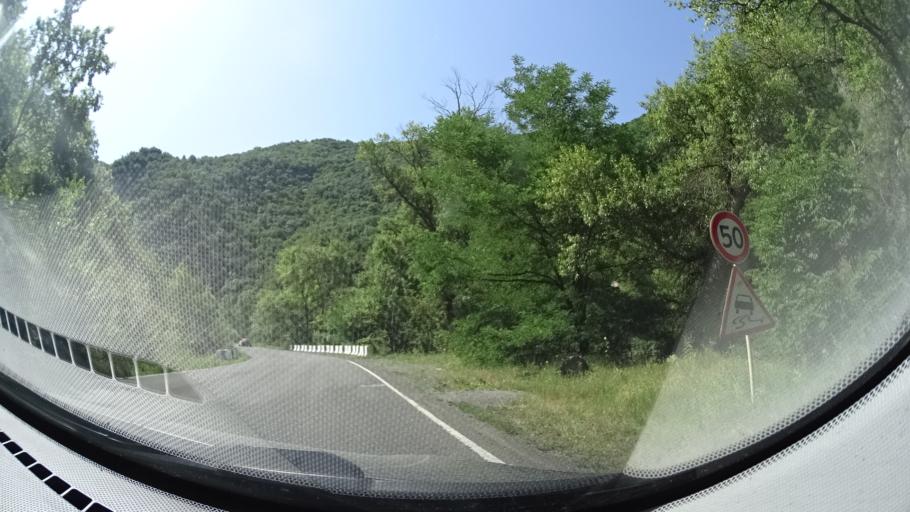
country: GE
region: Samtskhe-Javakheti
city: Akhaltsikhe
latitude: 41.6094
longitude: 43.0658
